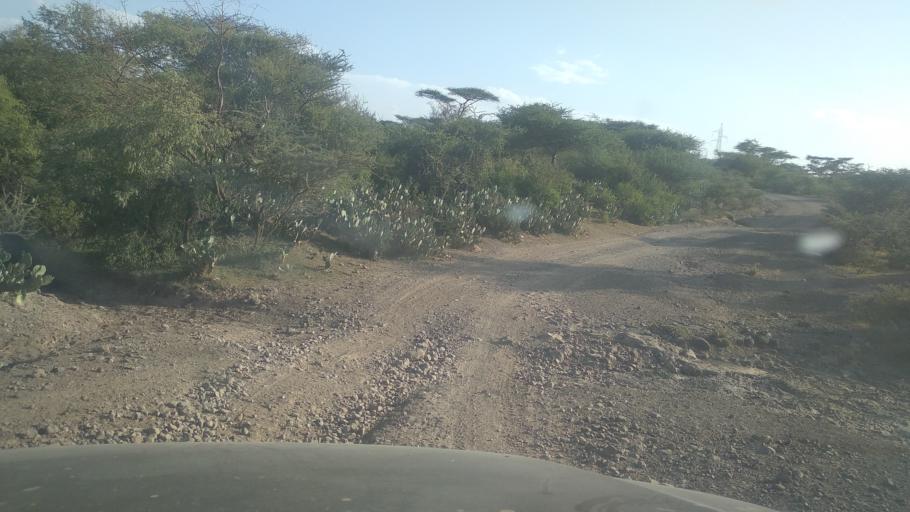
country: ET
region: Oromiya
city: Hirna
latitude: 9.4065
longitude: 40.9514
